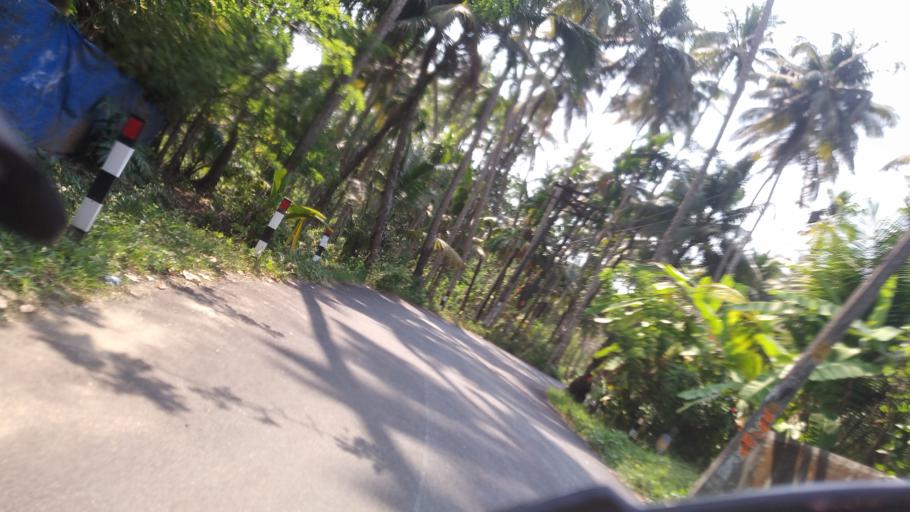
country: IN
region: Kerala
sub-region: Thrissur District
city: Thanniyam
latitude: 10.3573
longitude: 76.1102
